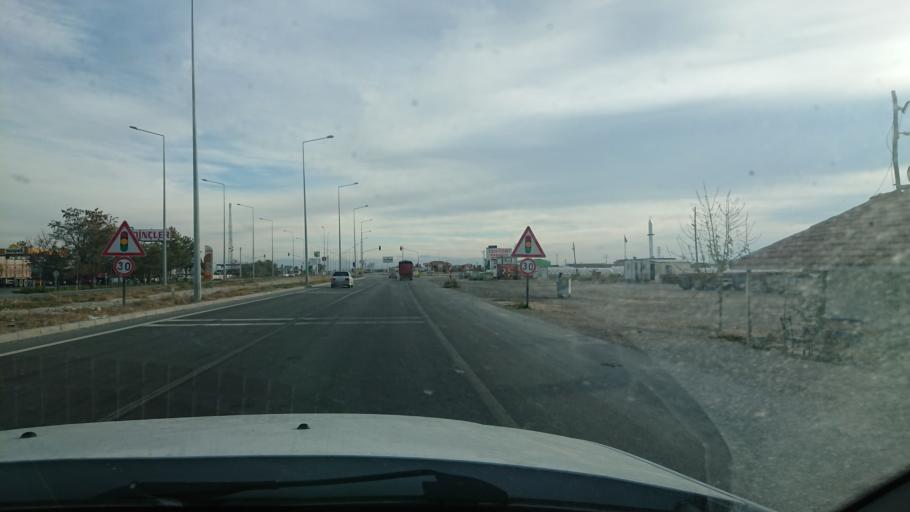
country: TR
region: Aksaray
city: Yesilova
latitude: 38.2907
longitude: 33.7585
